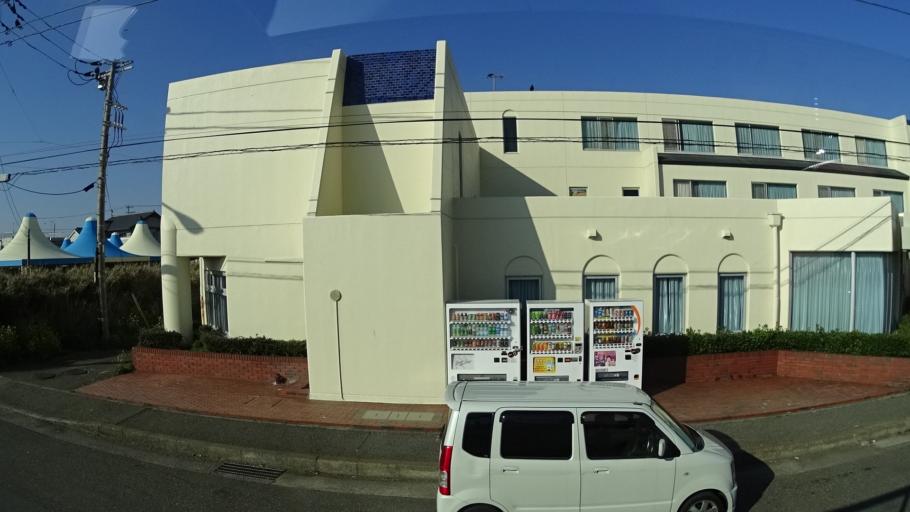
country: JP
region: Kanagawa
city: Miura
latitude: 35.1422
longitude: 139.6135
